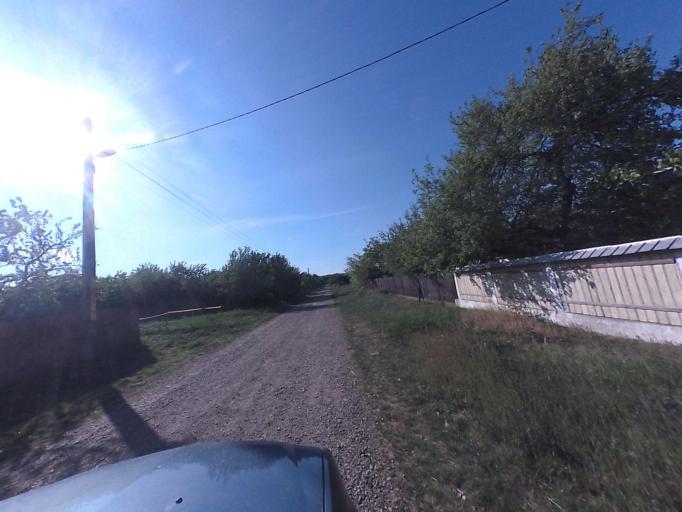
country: RO
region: Neamt
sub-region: Comuna Dulcesti
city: Dulcesti
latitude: 47.0051
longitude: 26.7709
